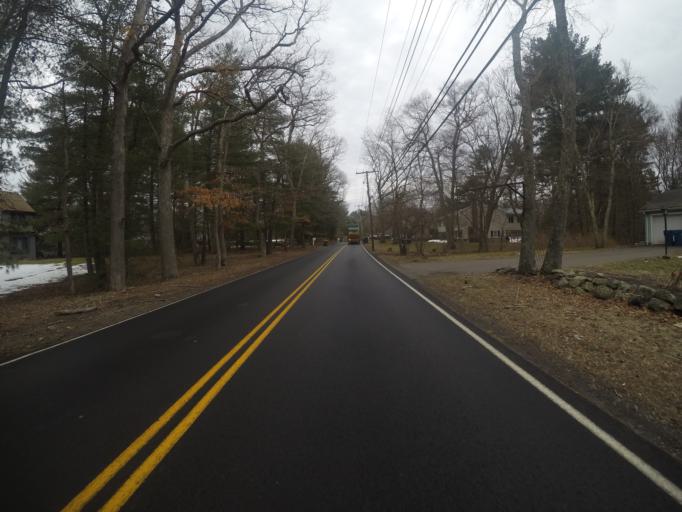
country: US
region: Massachusetts
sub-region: Bristol County
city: Easton
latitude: 42.0516
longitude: -71.1355
